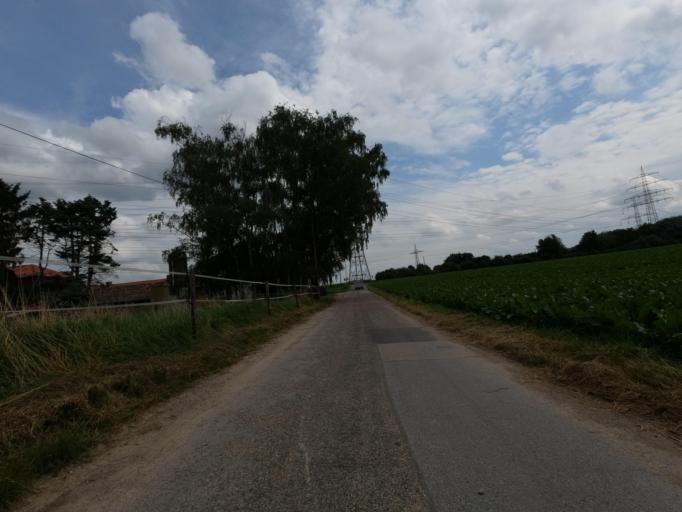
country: DE
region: North Rhine-Westphalia
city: Baesweiler
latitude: 50.9409
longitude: 6.2128
